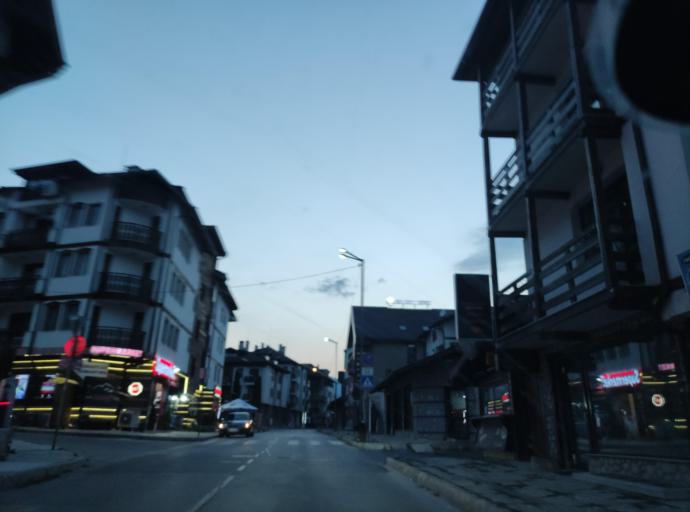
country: BG
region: Blagoevgrad
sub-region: Obshtina Bansko
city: Bansko
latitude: 41.8273
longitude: 23.4821
